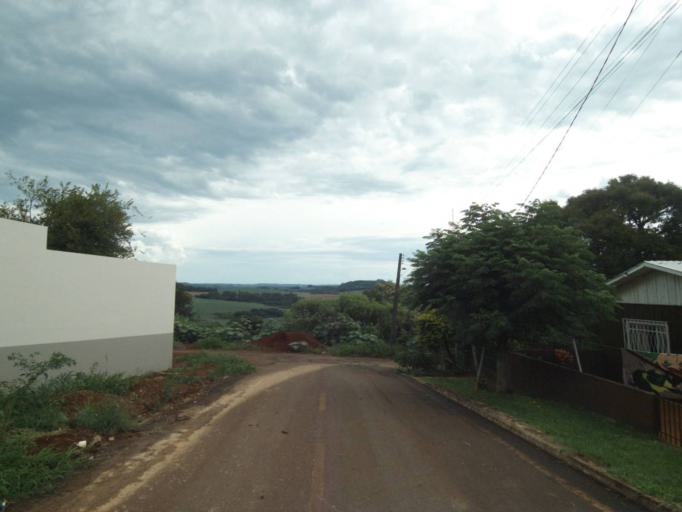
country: BR
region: Parana
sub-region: Guaraniacu
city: Guaraniacu
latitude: -25.1034
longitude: -52.8688
